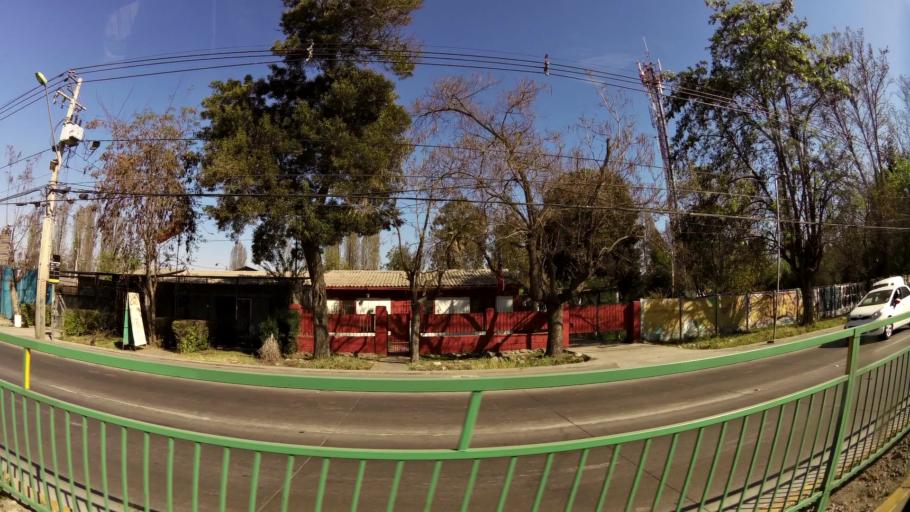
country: CL
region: Santiago Metropolitan
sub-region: Provincia de Santiago
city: La Pintana
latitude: -33.5850
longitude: -70.6235
